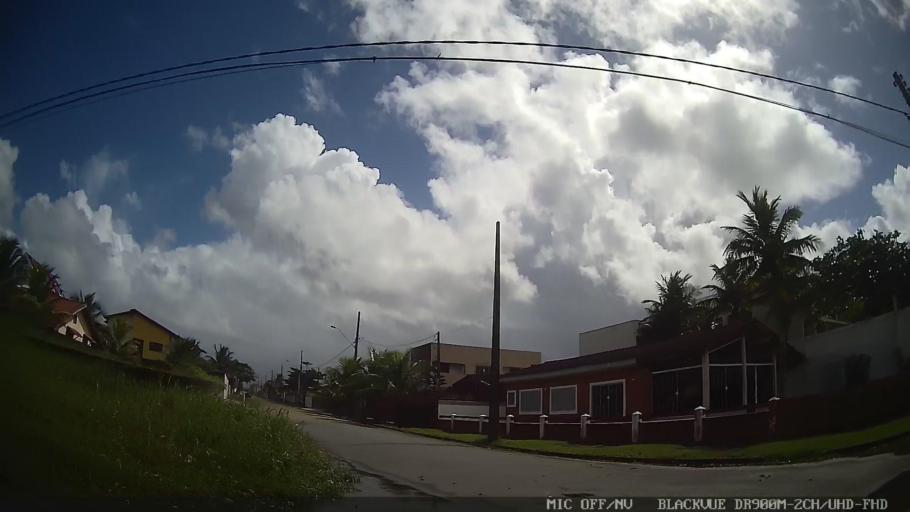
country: BR
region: Sao Paulo
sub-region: Itanhaem
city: Itanhaem
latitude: -24.2305
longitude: -46.8669
